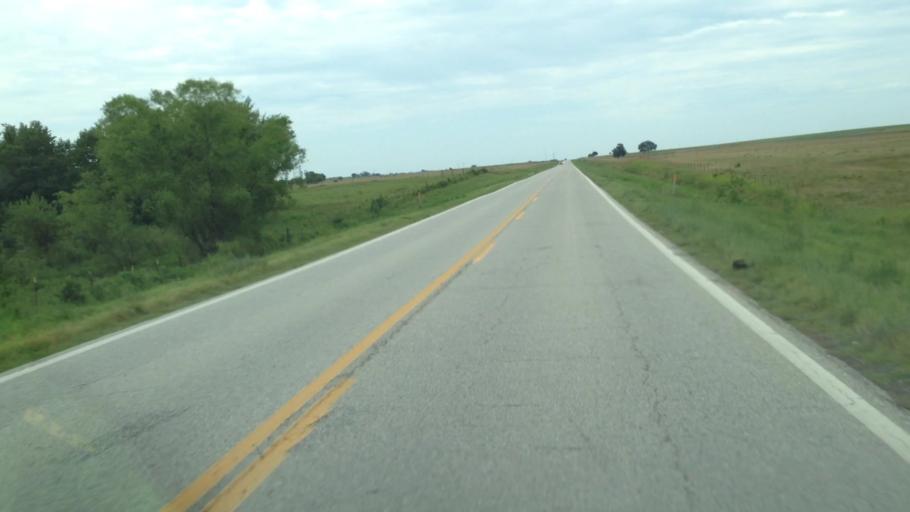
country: US
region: Oklahoma
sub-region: Craig County
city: Vinita
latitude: 36.8356
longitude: -95.1324
